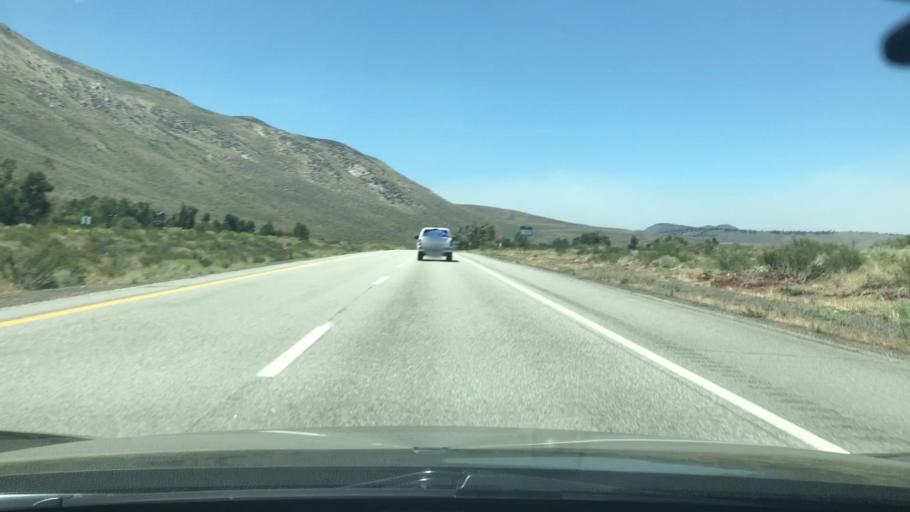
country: US
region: California
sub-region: Mono County
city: Mammoth Lakes
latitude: 37.5859
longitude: -118.7792
